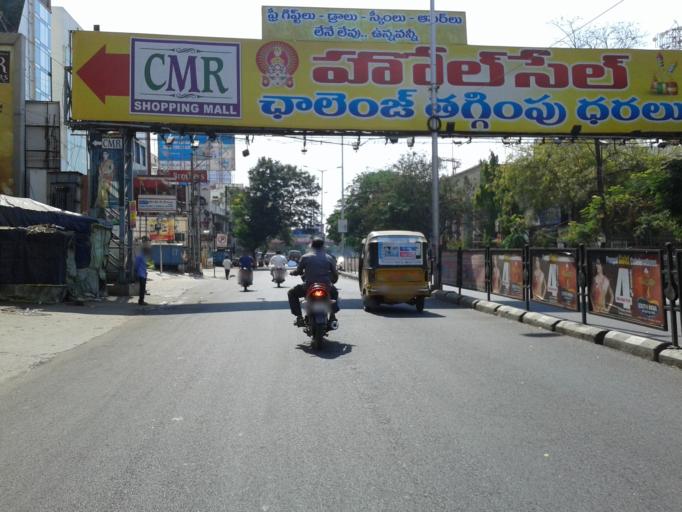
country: IN
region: Telangana
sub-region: Hyderabad
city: Malkajgiri
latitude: 17.4419
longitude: 78.4955
